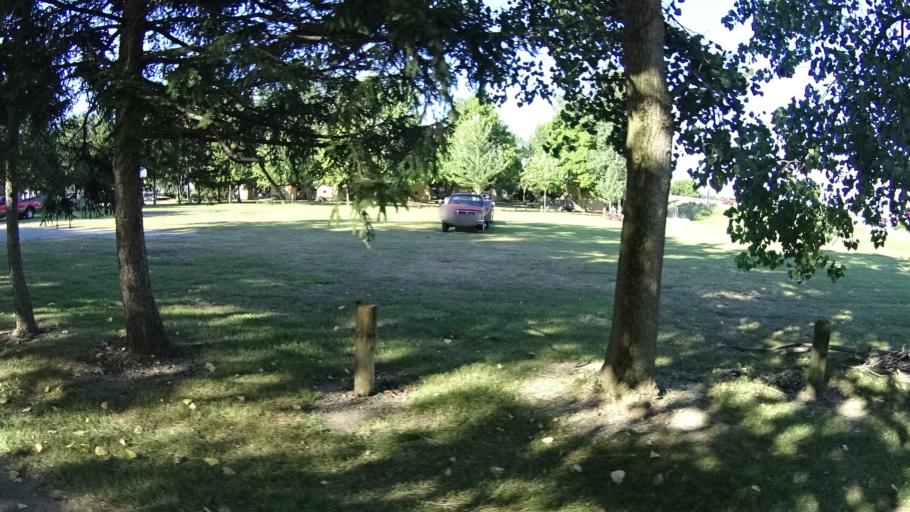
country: US
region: Ohio
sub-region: Erie County
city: Sandusky
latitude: 41.4206
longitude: -82.7560
